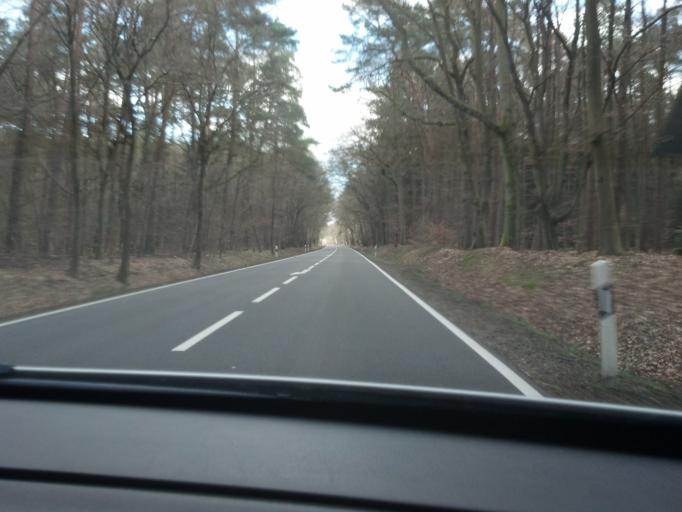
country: DE
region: Schleswig-Holstein
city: Langenlehsten
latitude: 53.4435
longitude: 10.7567
